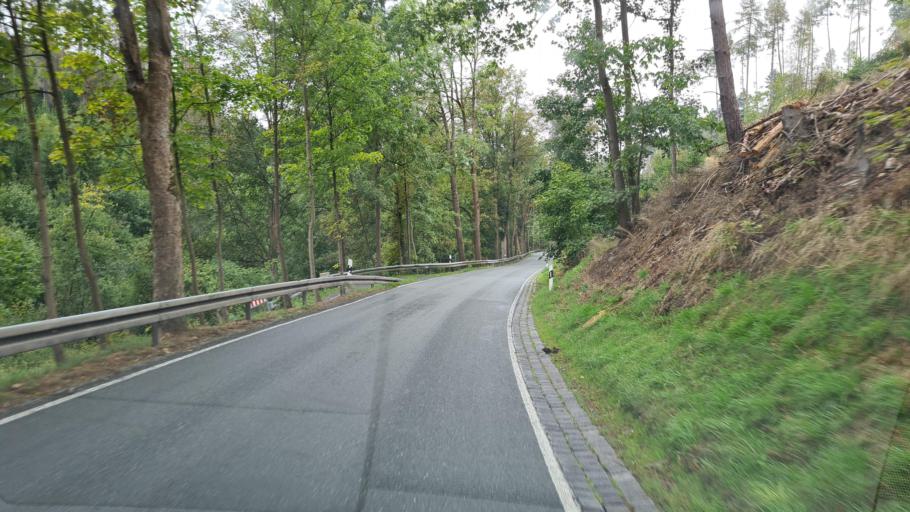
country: DE
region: Thuringia
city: Leutenberg
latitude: 50.5291
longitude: 11.5016
